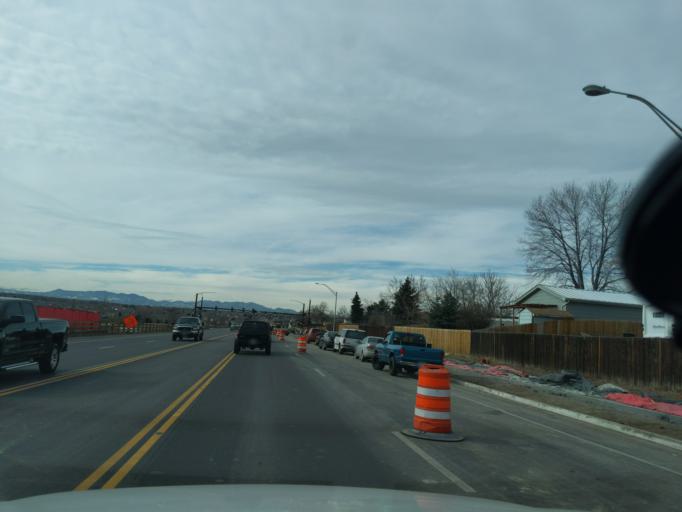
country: US
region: Colorado
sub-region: Adams County
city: Thornton
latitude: 39.8994
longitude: -104.9428
